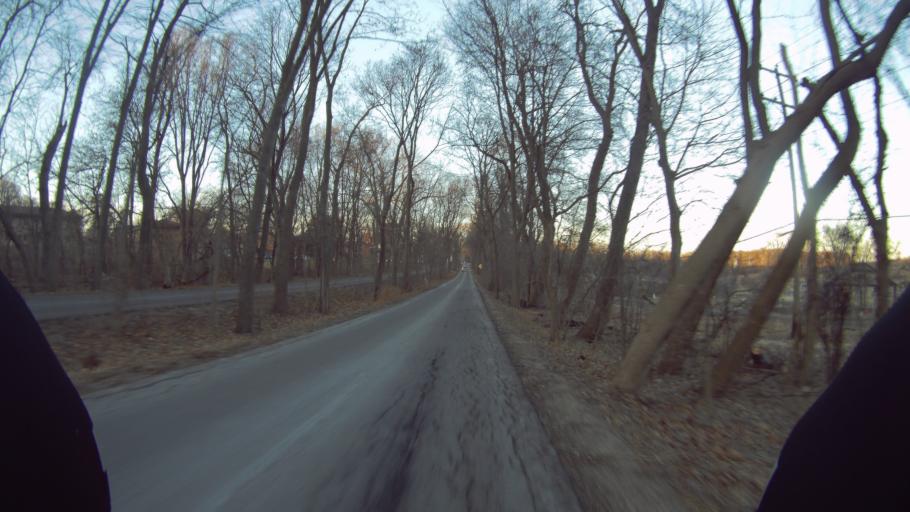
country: US
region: Wisconsin
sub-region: Dane County
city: Shorewood Hills
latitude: 43.0870
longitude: -89.4336
